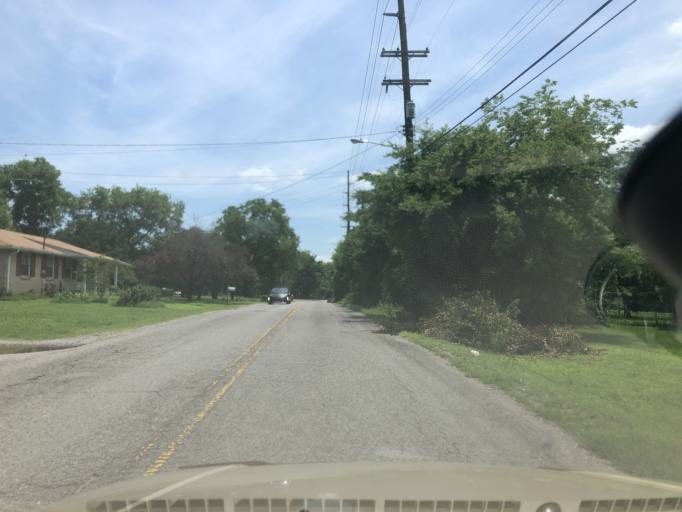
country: US
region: Tennessee
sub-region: Davidson County
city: Goodlettsville
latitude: 36.2568
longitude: -86.7042
